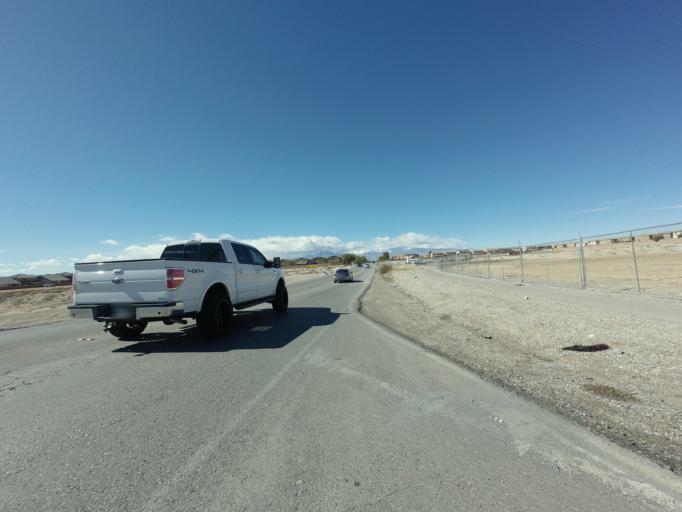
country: US
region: Nevada
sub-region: Clark County
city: Nellis Air Force Base
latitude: 36.2693
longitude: -115.0807
